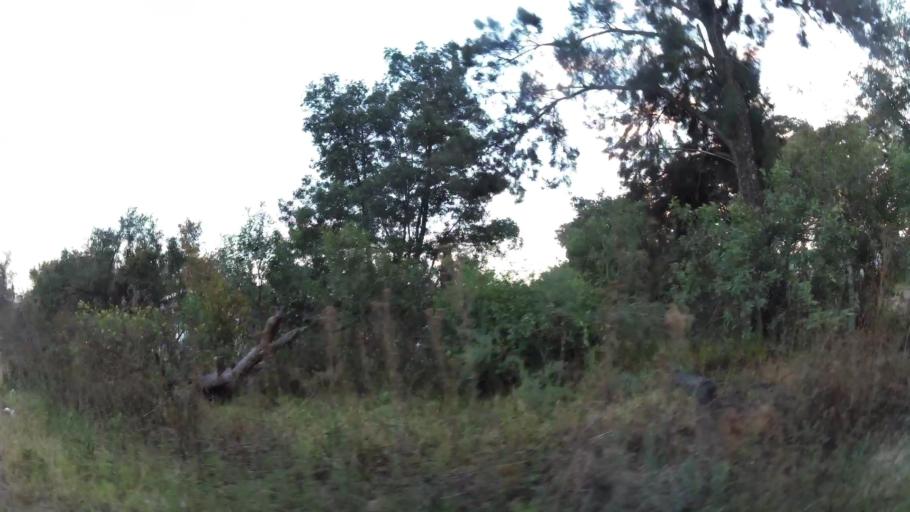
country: ZA
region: Gauteng
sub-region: City of Johannesburg Metropolitan Municipality
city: Midrand
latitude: -26.0100
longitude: 28.0556
